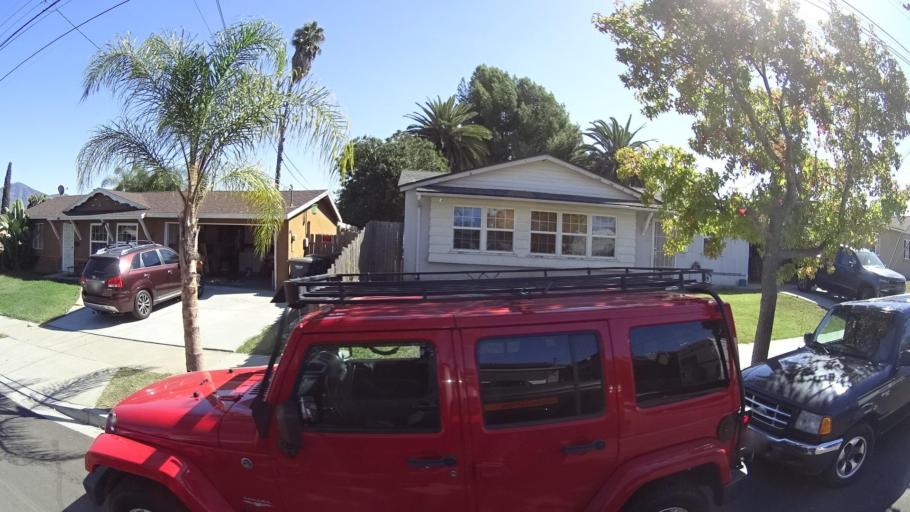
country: US
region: California
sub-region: San Diego County
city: La Presa
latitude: 32.7063
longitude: -117.0171
